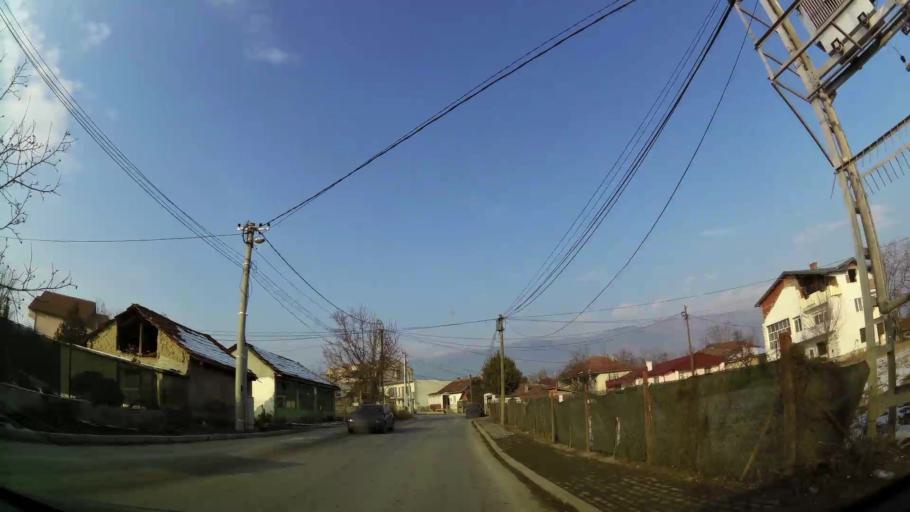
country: MK
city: Creshevo
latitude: 42.0252
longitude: 21.5150
